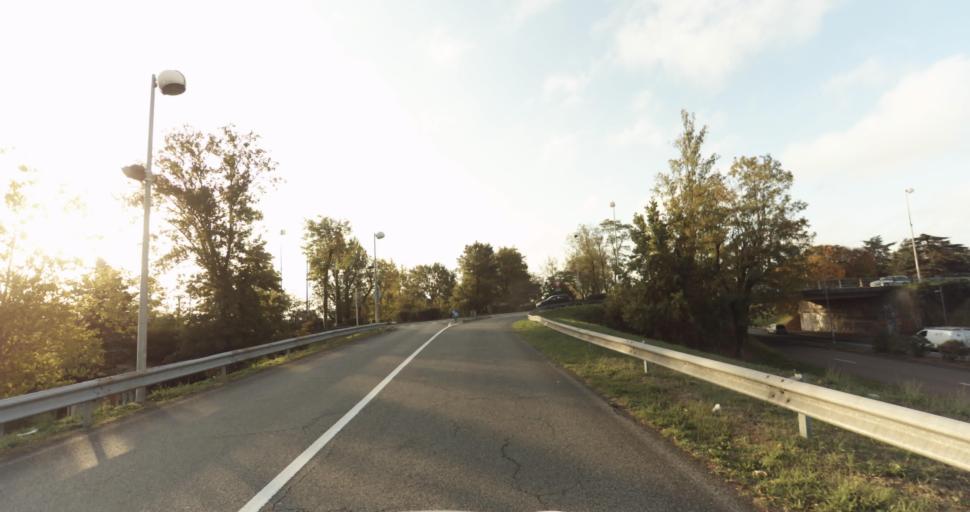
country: FR
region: Midi-Pyrenees
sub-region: Departement de la Haute-Garonne
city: Ramonville-Saint-Agne
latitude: 43.5485
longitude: 1.4800
